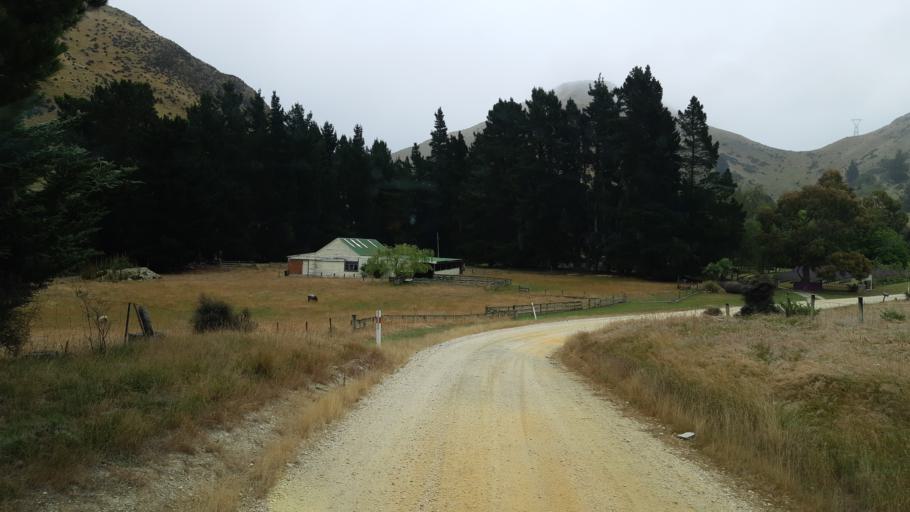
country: NZ
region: Otago
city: Oamaru
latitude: -44.9542
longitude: 170.4759
